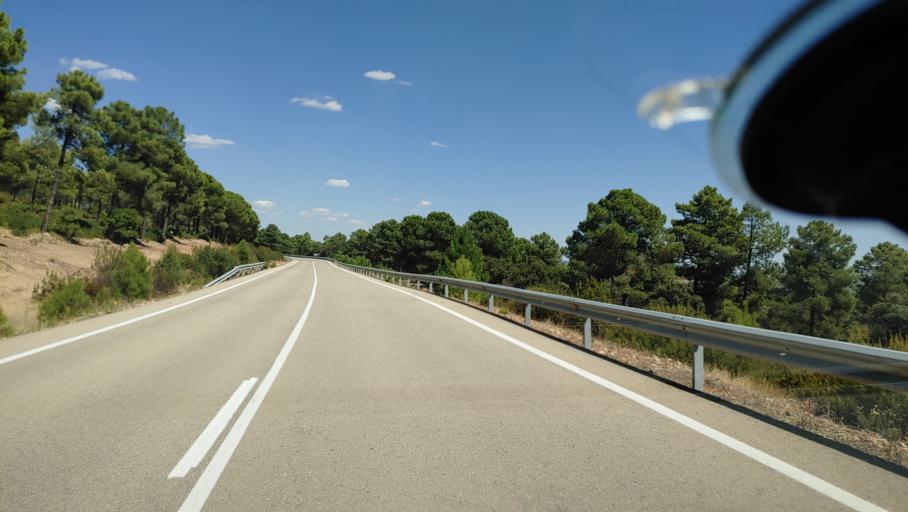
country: ES
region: Castille-La Mancha
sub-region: Provincia de Ciudad Real
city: Saceruela
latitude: 38.9930
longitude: -4.5216
